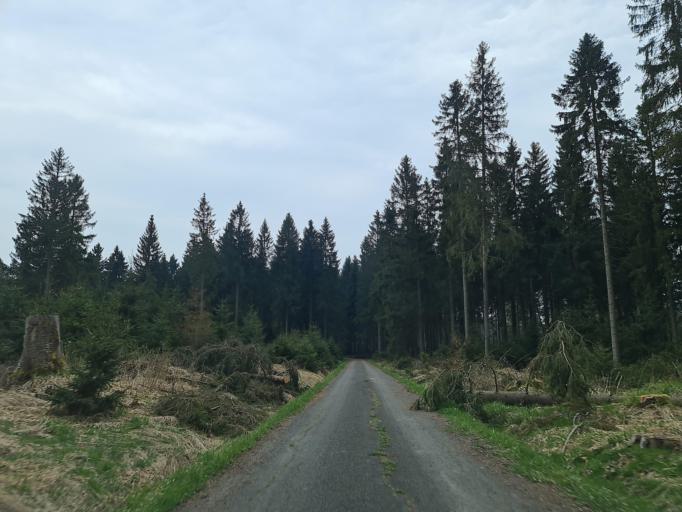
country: DE
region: Saxony
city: Grunbach
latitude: 50.4540
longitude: 12.3854
